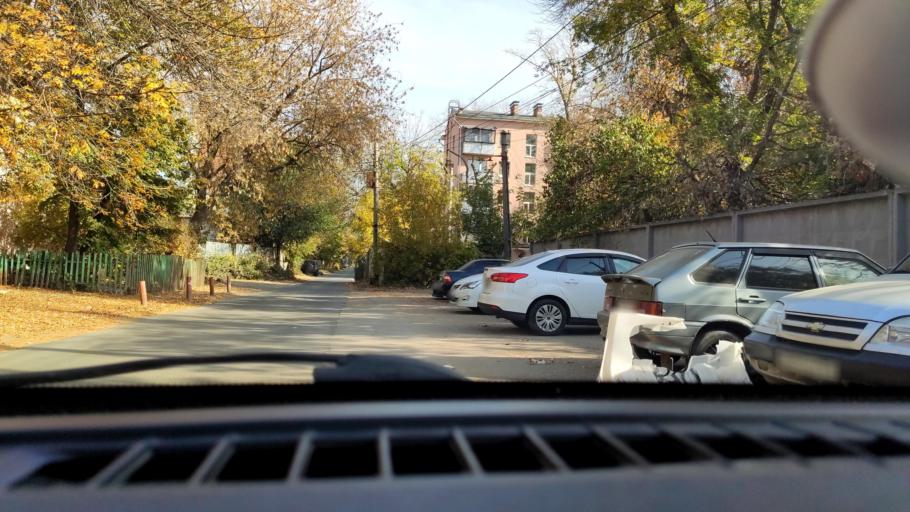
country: RU
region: Samara
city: Samara
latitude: 53.2015
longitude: 50.1811
